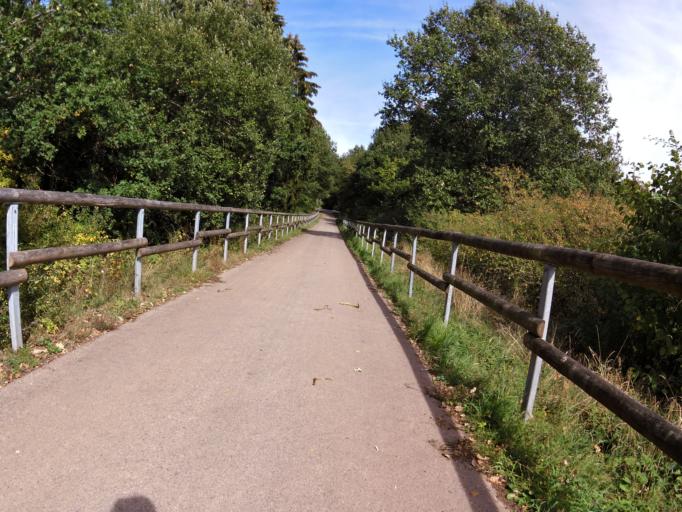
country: DE
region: Rheinland-Pfalz
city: Strickscheid
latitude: 50.1389
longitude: 6.3246
